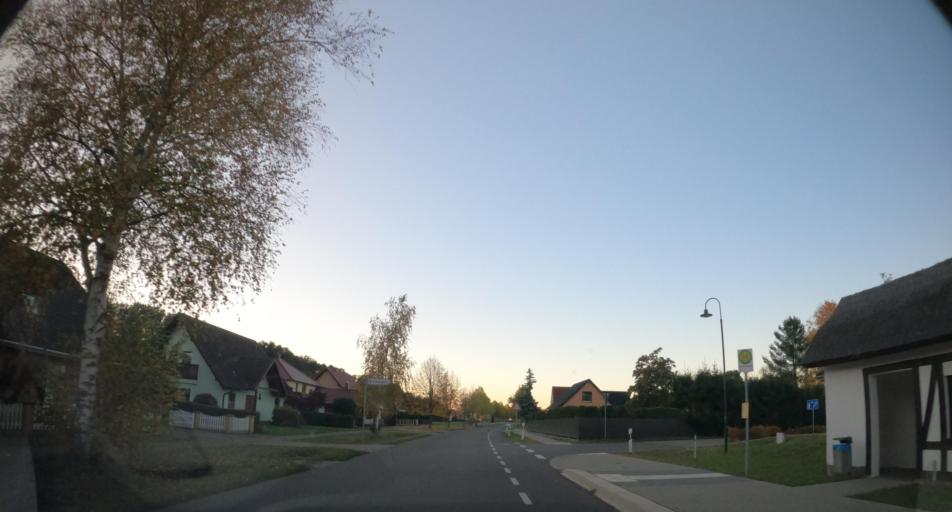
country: DE
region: Mecklenburg-Vorpommern
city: Ueckermunde
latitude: 53.7595
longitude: 14.0103
